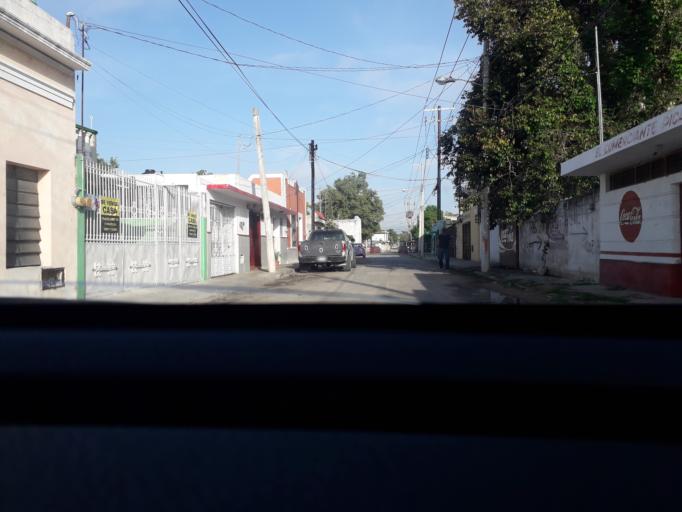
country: MX
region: Yucatan
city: Merida
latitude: 20.9607
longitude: -89.6325
